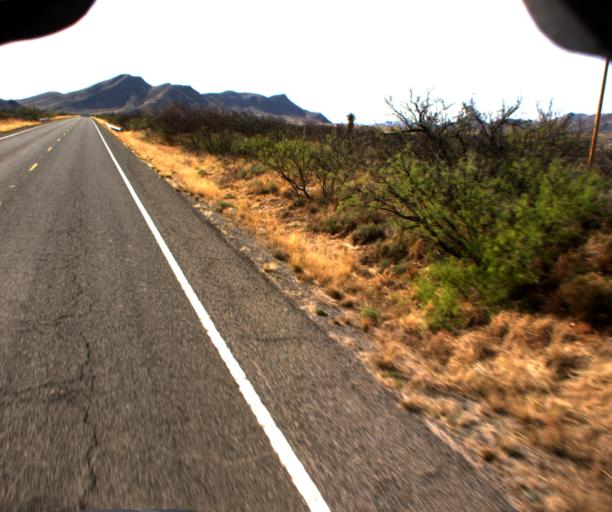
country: US
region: Arizona
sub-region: Cochise County
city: Willcox
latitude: 32.1770
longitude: -109.6243
